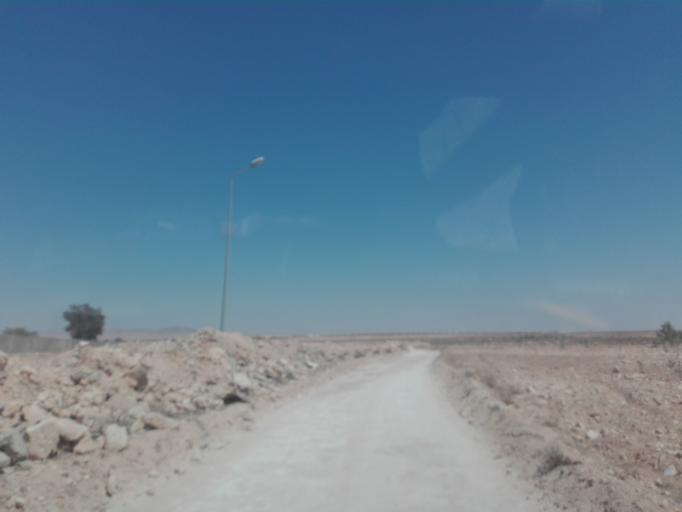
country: TN
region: Safaqis
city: Skhira
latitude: 34.4153
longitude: 9.9513
